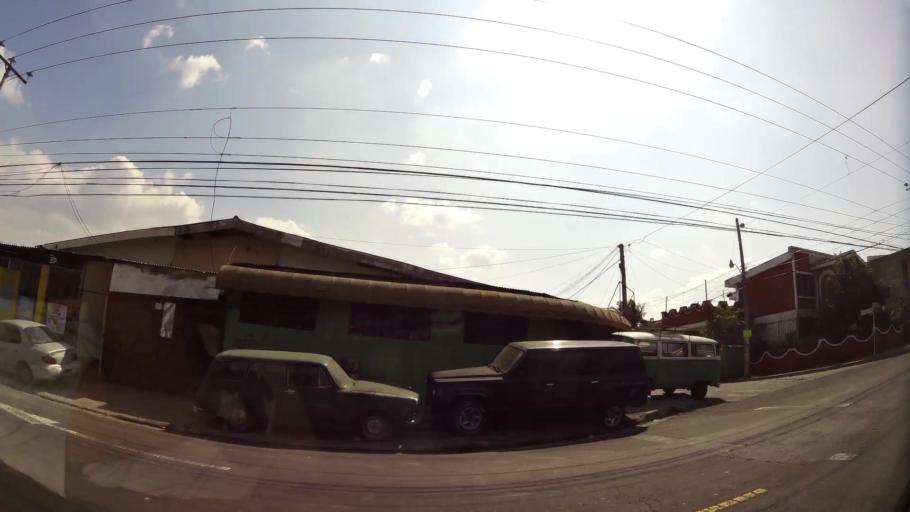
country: SV
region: San Salvador
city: Mejicanos
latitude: 13.7230
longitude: -89.2194
